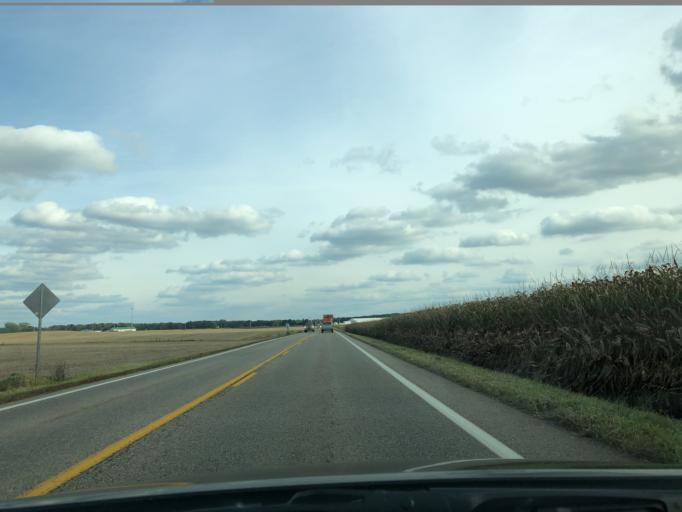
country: US
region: Ohio
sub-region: Stark County
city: Beach City
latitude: 40.6467
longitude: -81.5916
